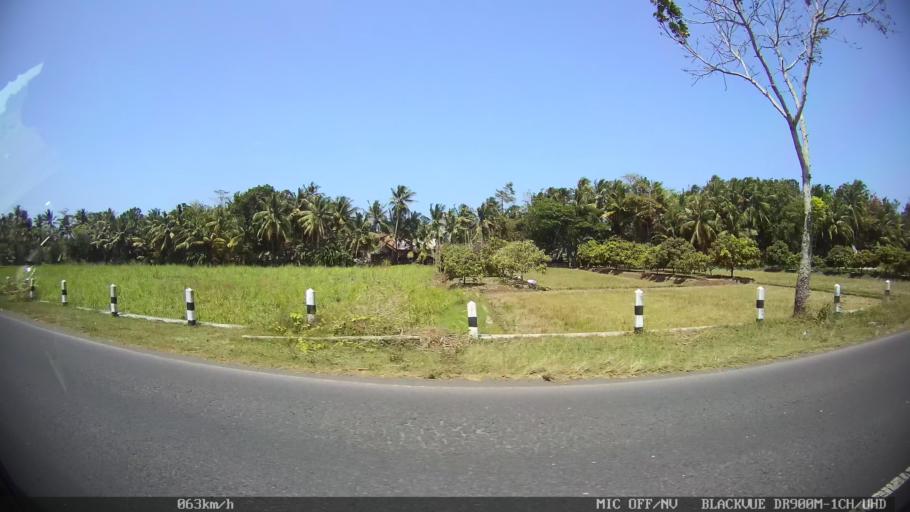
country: ID
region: Daerah Istimewa Yogyakarta
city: Srandakan
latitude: -7.9416
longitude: 110.1642
